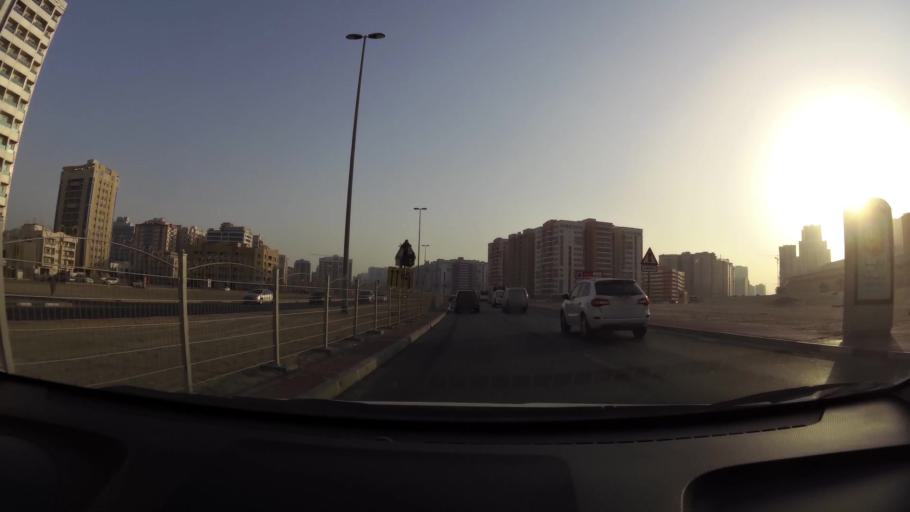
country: AE
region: Ash Shariqah
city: Sharjah
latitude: 25.2968
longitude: 55.3755
